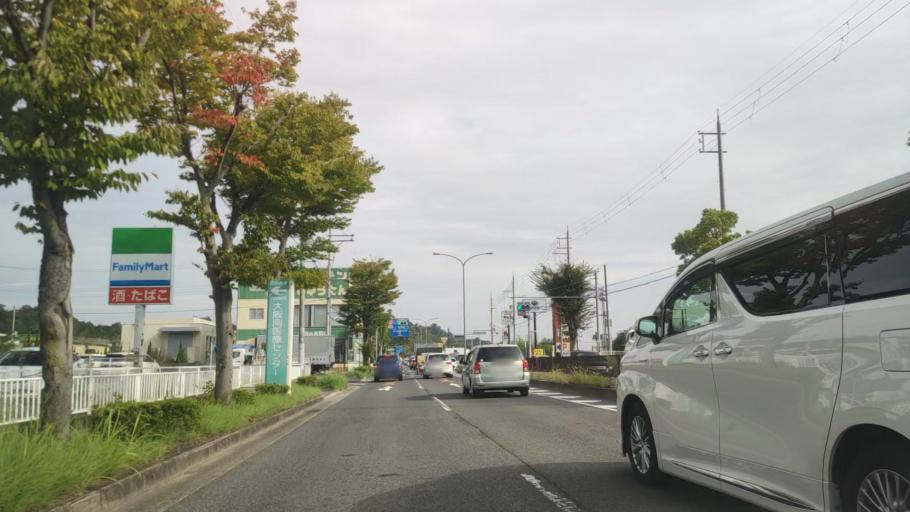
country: JP
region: Osaka
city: Tondabayashicho
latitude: 34.4738
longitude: 135.5757
